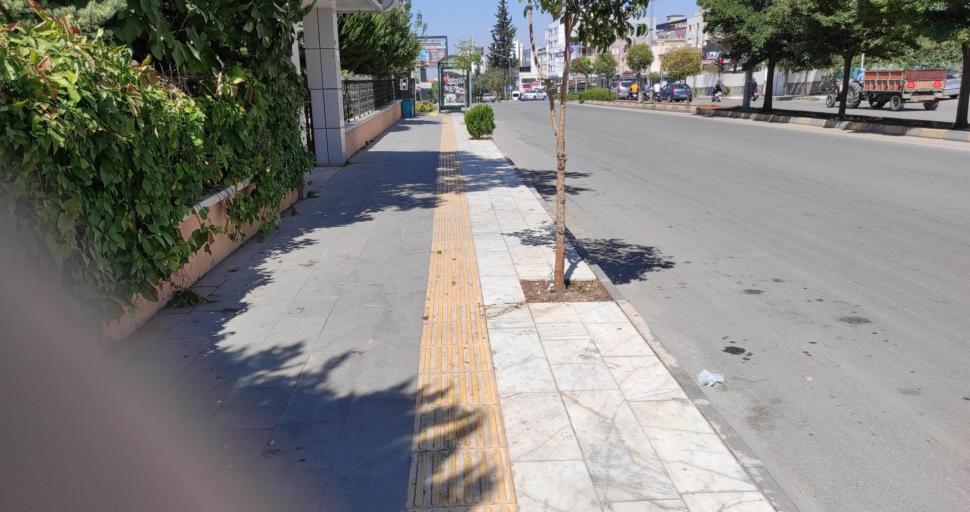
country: TR
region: Kilis
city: Kilis
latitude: 36.7266
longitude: 37.1019
